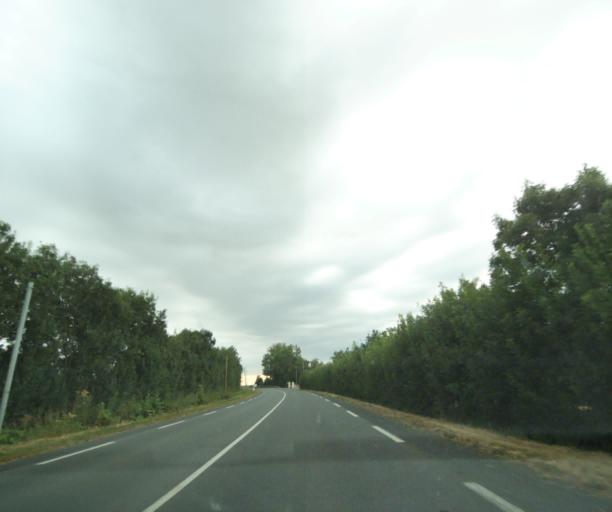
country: FR
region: Pays de la Loire
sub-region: Departement de la Vendee
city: Chaille-les-Marais
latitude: 46.4116
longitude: -1.0410
